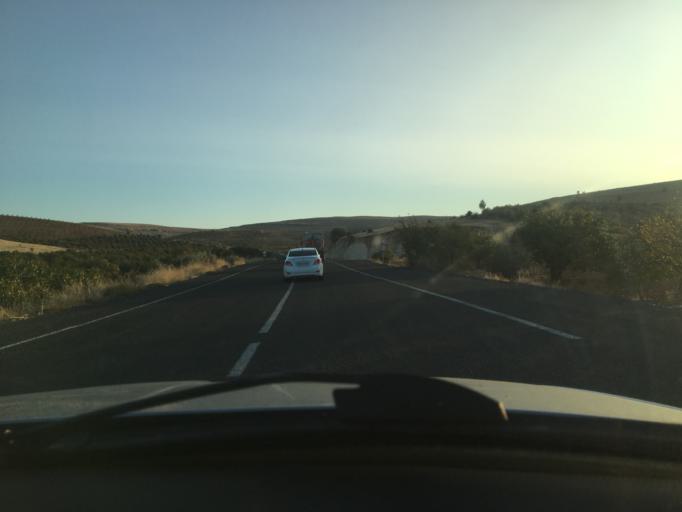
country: TR
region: Sanliurfa
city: Halfeti
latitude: 37.1985
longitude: 37.9673
